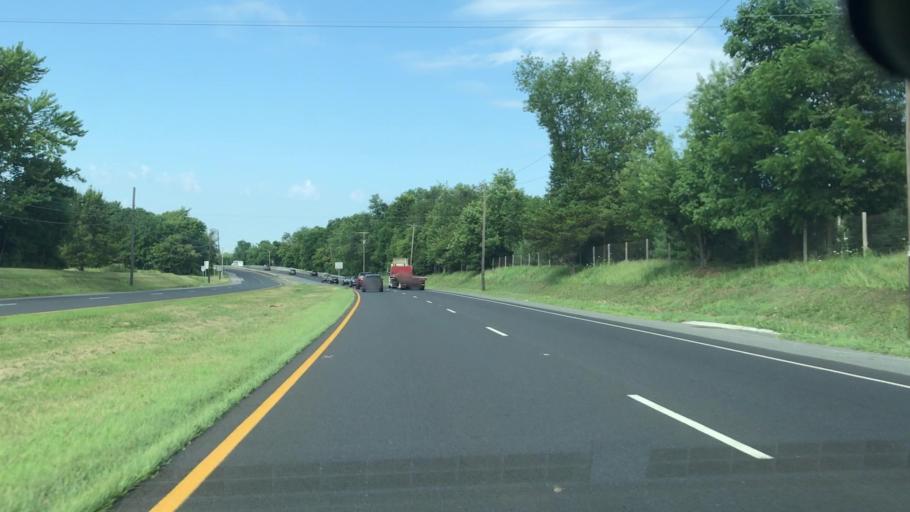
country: US
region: New Jersey
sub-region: Hunterdon County
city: Flemington
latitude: 40.5245
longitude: -74.8043
